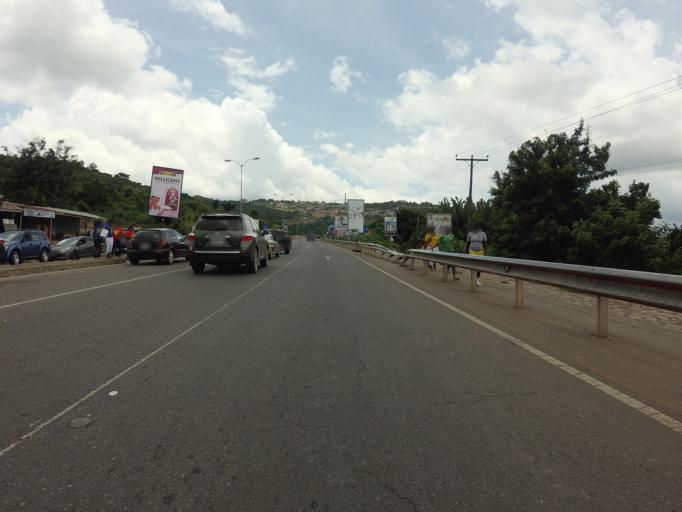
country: GH
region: Eastern
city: Aburi
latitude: 5.7861
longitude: -0.1831
